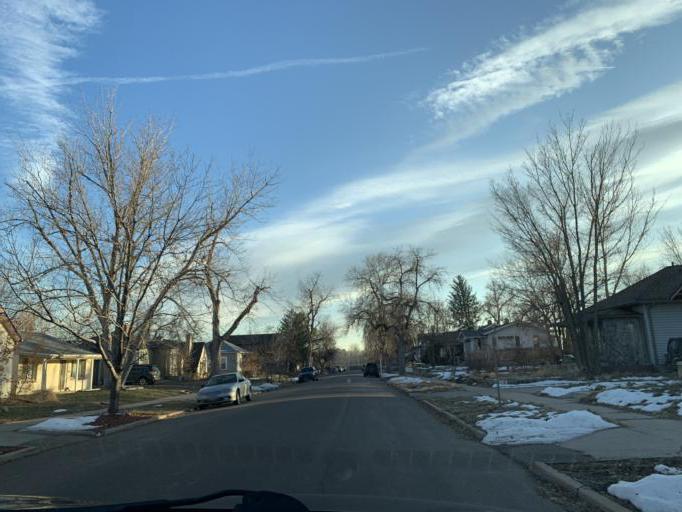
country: US
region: Colorado
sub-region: Adams County
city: Berkley
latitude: 39.7865
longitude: -105.0311
